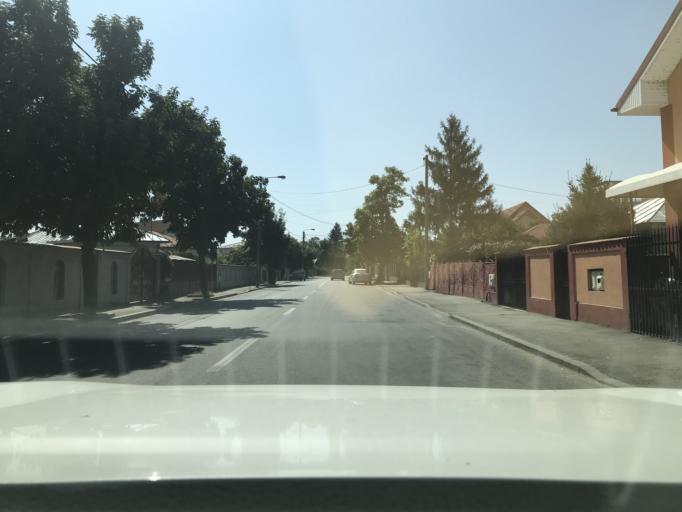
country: RO
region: Olt
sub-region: Municipiul Slatina
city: Slatina
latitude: 44.4209
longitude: 24.3620
